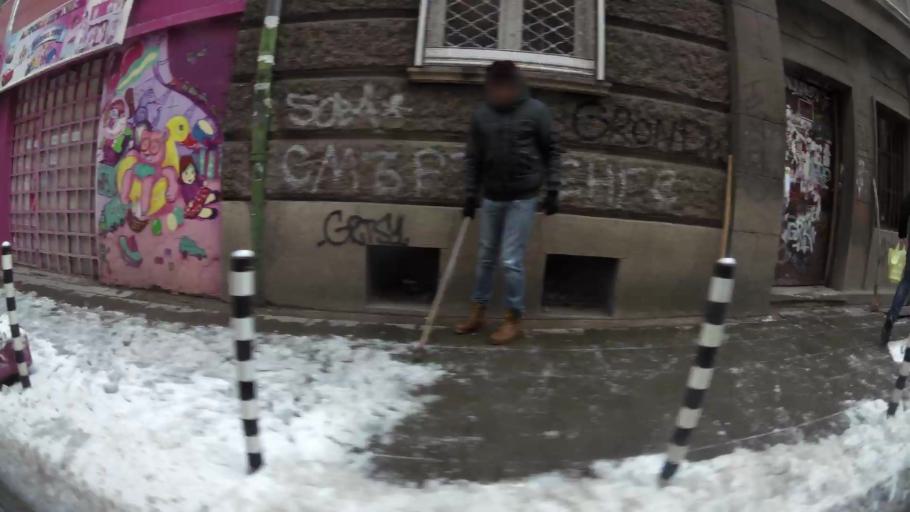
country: BG
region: Sofia-Capital
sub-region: Stolichna Obshtina
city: Sofia
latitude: 42.6896
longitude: 23.3303
